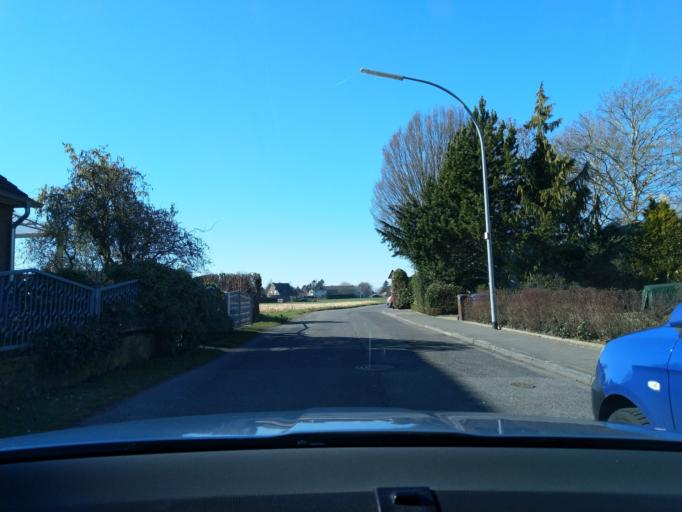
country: DE
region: North Rhine-Westphalia
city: Erkelenz
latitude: 51.1068
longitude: 6.3794
